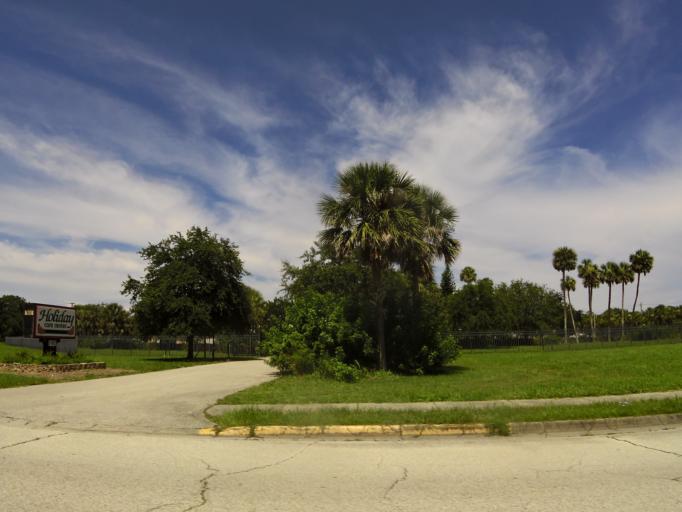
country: US
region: Florida
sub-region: Volusia County
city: Daytona Beach
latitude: 29.1928
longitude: -81.0104
